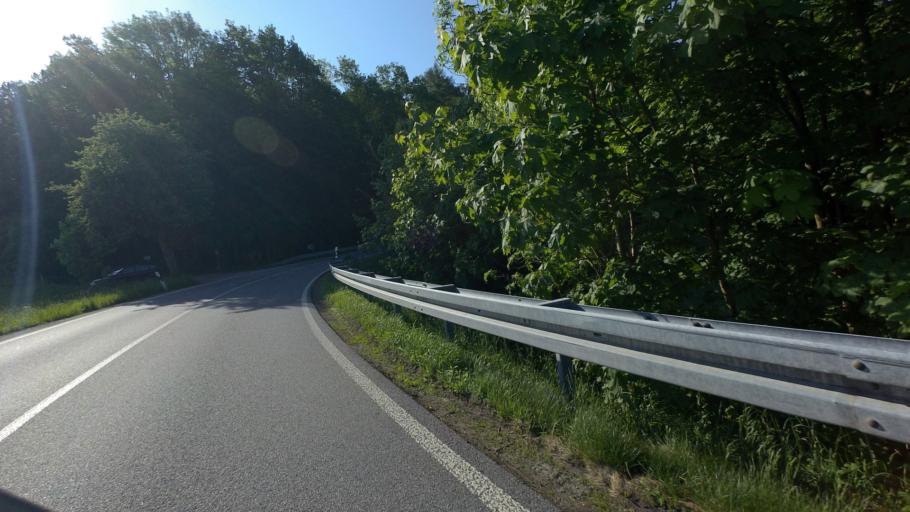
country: DE
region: Saxony
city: Sebnitz
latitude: 50.9617
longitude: 14.2456
